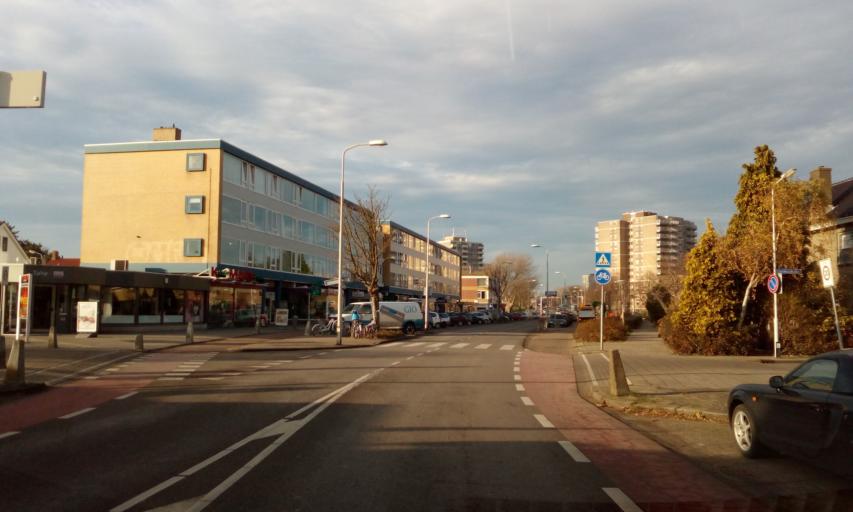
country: NL
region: South Holland
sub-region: Gemeente Zoetermeer
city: Zoetermeer
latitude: 52.0523
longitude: 4.4962
